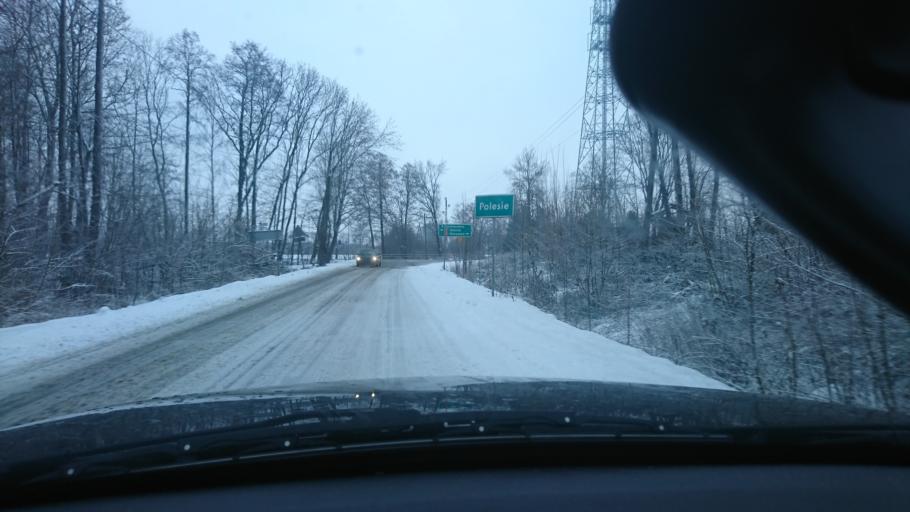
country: PL
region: Masovian Voivodeship
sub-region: Powiat ciechanowski
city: Glinojeck
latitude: 52.7515
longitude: 20.3132
